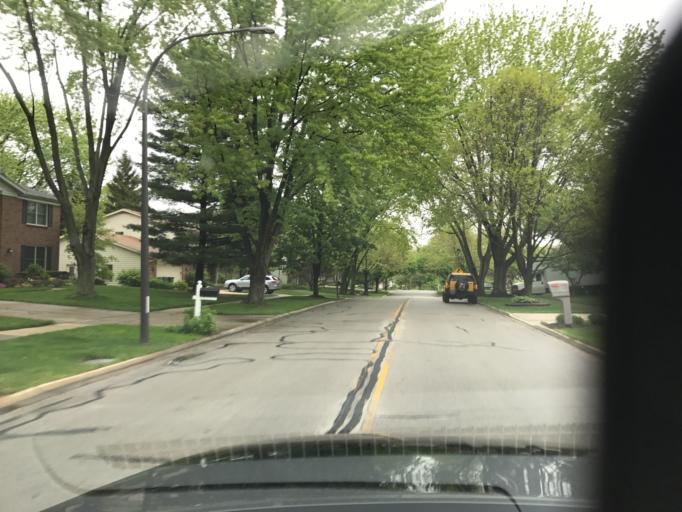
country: US
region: Illinois
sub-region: DuPage County
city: Naperville
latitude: 41.7619
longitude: -88.1212
